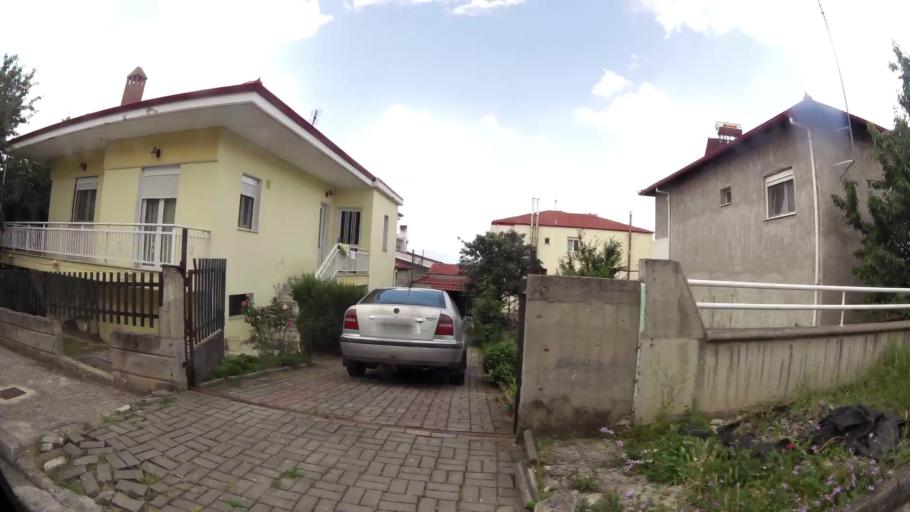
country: GR
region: West Macedonia
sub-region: Nomos Kozanis
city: Koila
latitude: 40.3276
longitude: 21.8206
